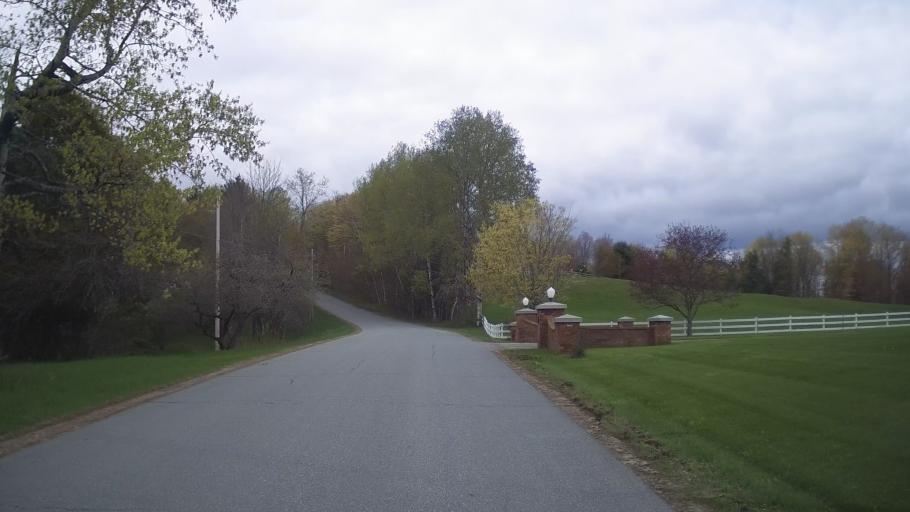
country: US
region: Vermont
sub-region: Caledonia County
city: Lyndonville
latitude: 44.5953
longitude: -71.9564
